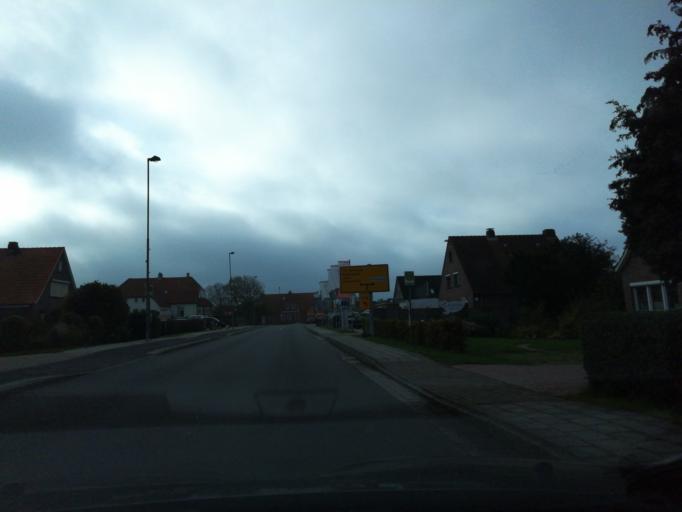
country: DE
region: Lower Saxony
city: Werdum
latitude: 53.6923
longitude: 7.8065
